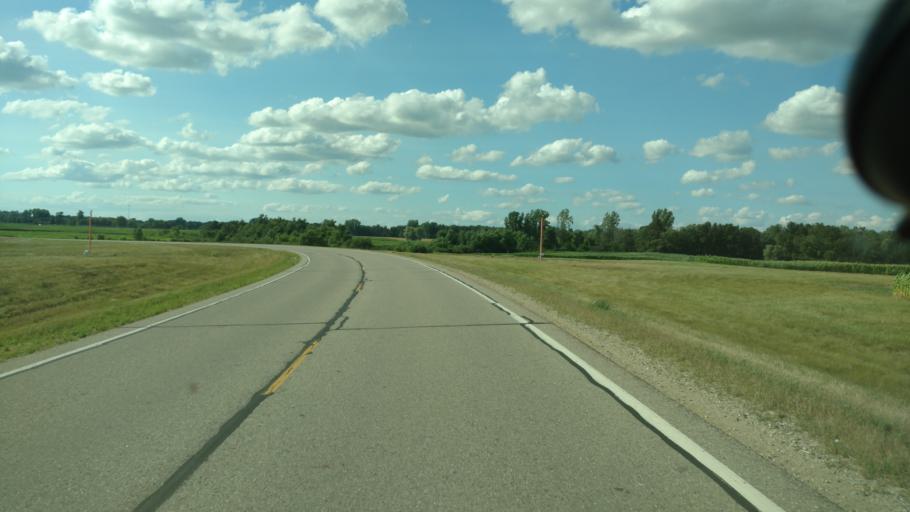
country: US
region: Michigan
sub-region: Ingham County
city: Edgemont Park
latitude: 42.7772
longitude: -84.5627
